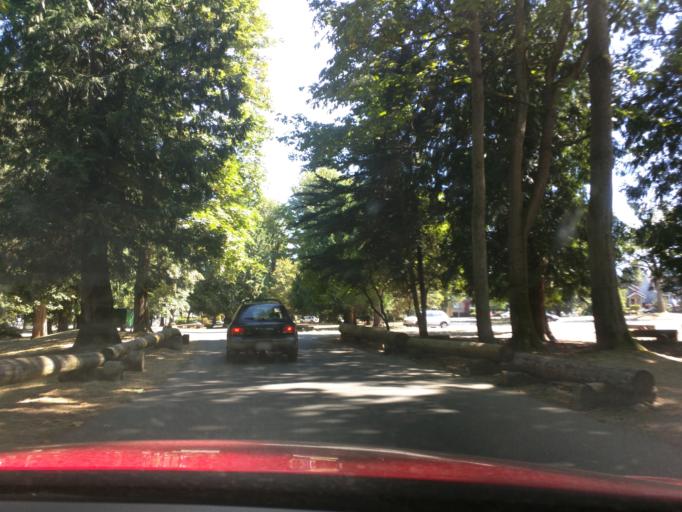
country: US
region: Washington
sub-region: King County
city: Seattle
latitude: 47.6663
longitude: -122.3457
